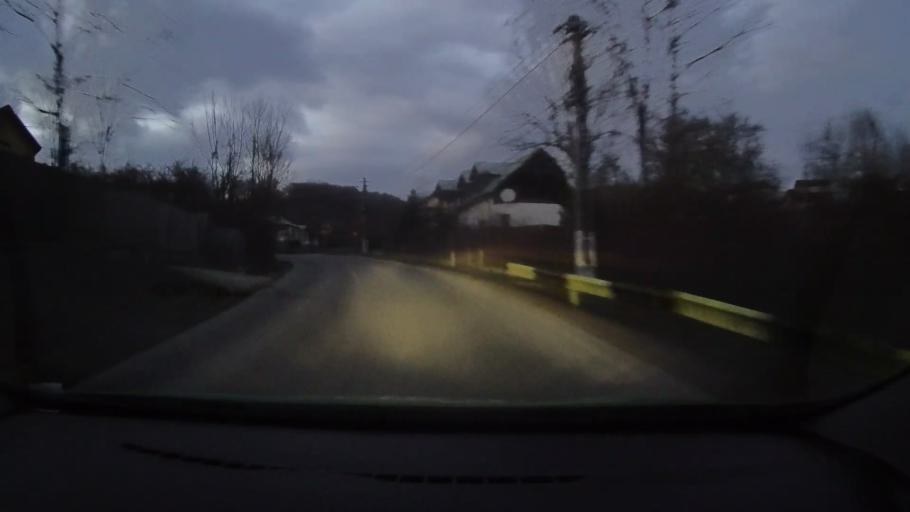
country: RO
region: Prahova
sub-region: Comuna Poiana Campina
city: Poiana Campina
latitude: 45.1259
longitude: 25.6779
